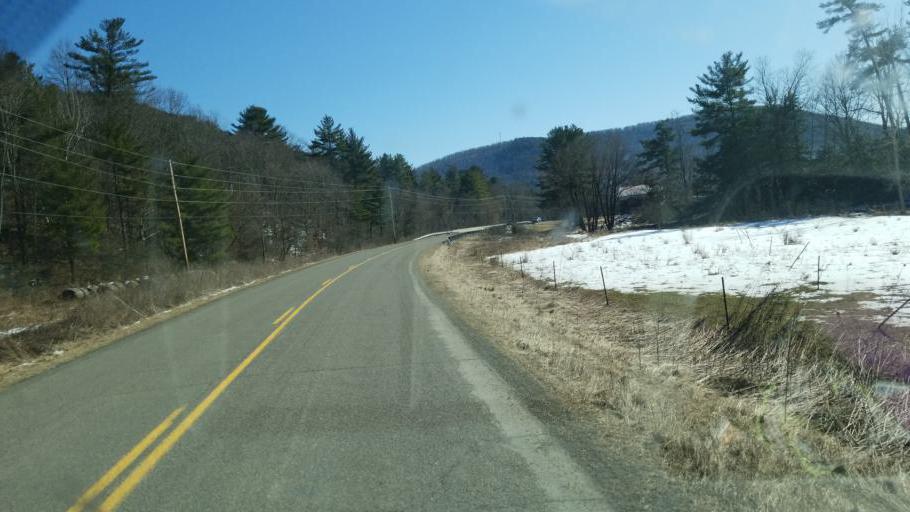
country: US
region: Pennsylvania
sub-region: Tioga County
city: Westfield
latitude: 41.9309
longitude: -77.5663
